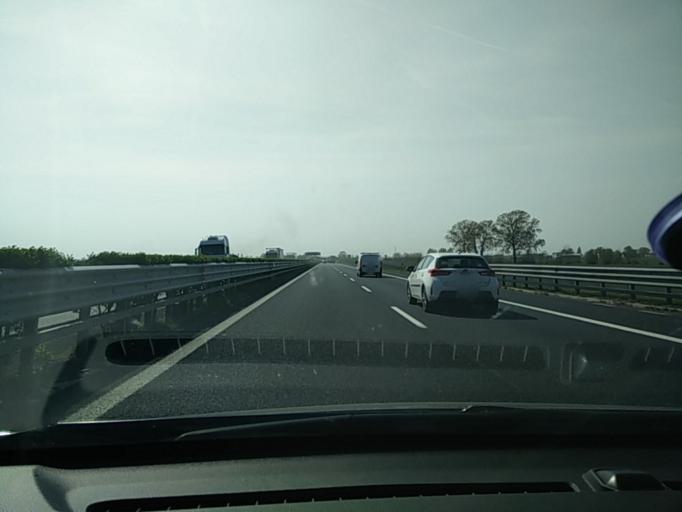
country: IT
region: Veneto
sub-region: Provincia di Venezia
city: San Giorgio al Tagliamento-Pozzi
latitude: 45.8083
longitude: 12.9513
